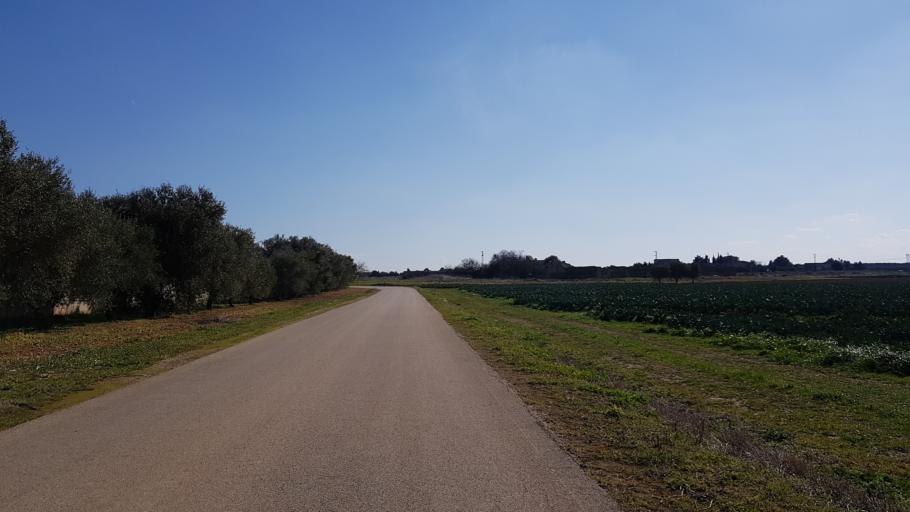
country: IT
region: Apulia
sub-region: Provincia di Brindisi
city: Mesagne
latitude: 40.6186
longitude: 17.8168
